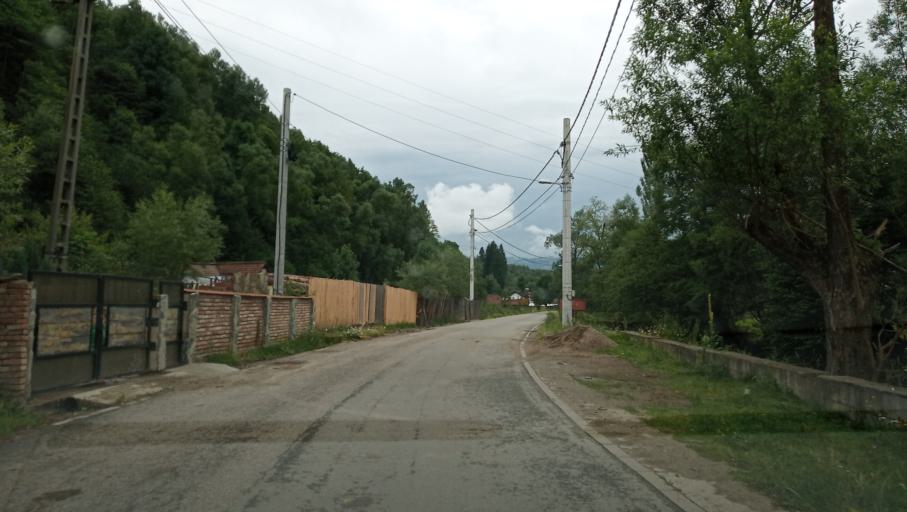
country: RO
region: Hunedoara
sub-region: Oras Petrila
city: Petrila
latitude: 45.4655
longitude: 23.4199
